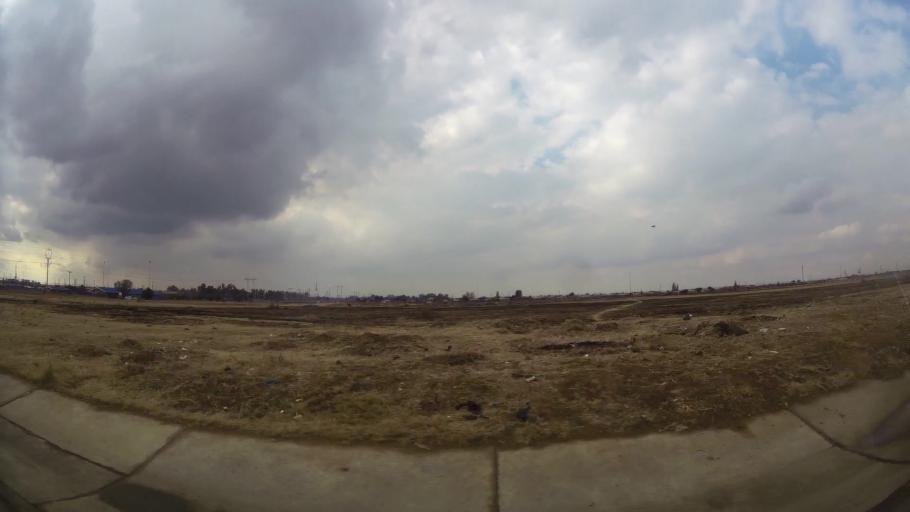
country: ZA
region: Orange Free State
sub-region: Fezile Dabi District Municipality
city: Sasolburg
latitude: -26.8572
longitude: 27.8669
